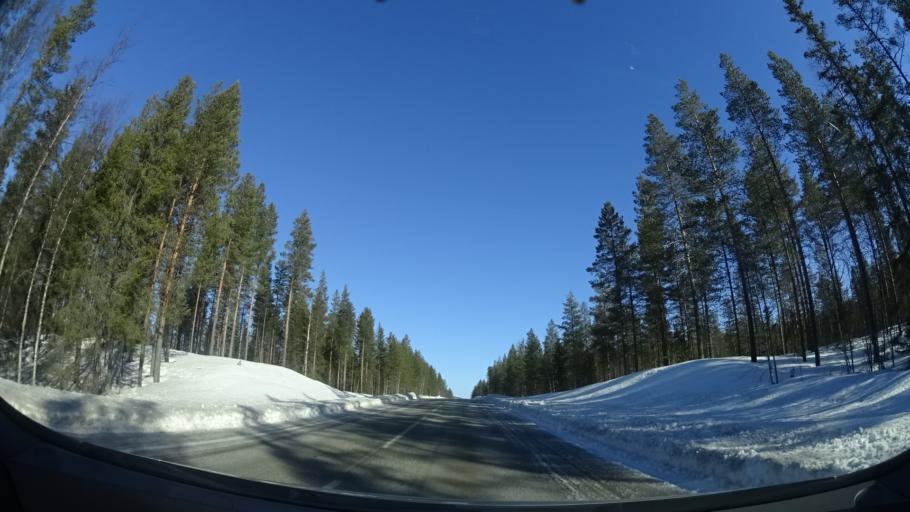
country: SE
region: Vaesterbotten
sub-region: Skelleftea Kommun
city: Langsele
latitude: 65.0878
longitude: 20.0794
